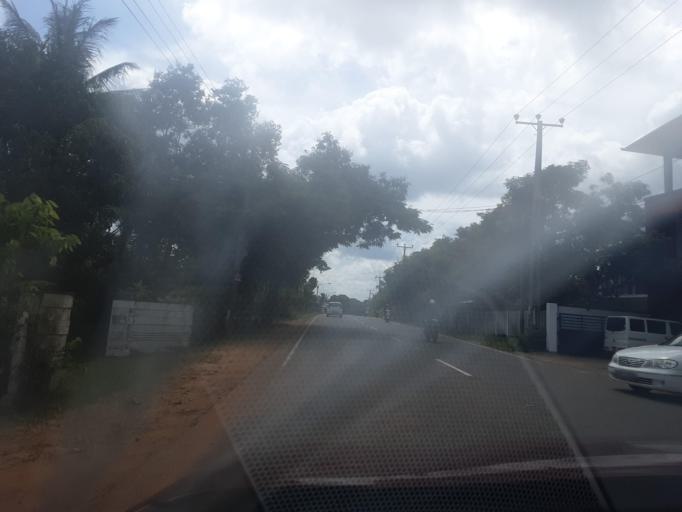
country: LK
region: North Western
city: Kuliyapitiya
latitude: 7.4754
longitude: 80.0149
